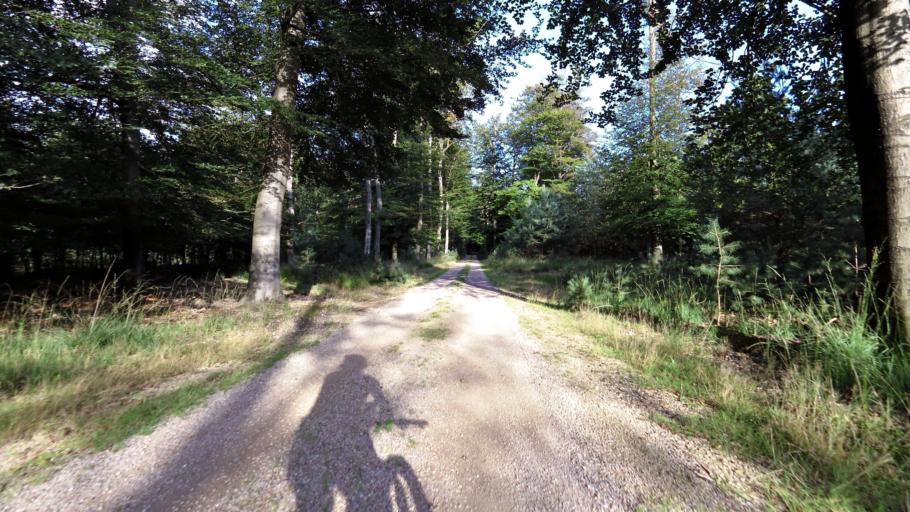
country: NL
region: Gelderland
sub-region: Gemeente Apeldoorn
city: Uddel
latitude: 52.2677
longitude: 5.8473
